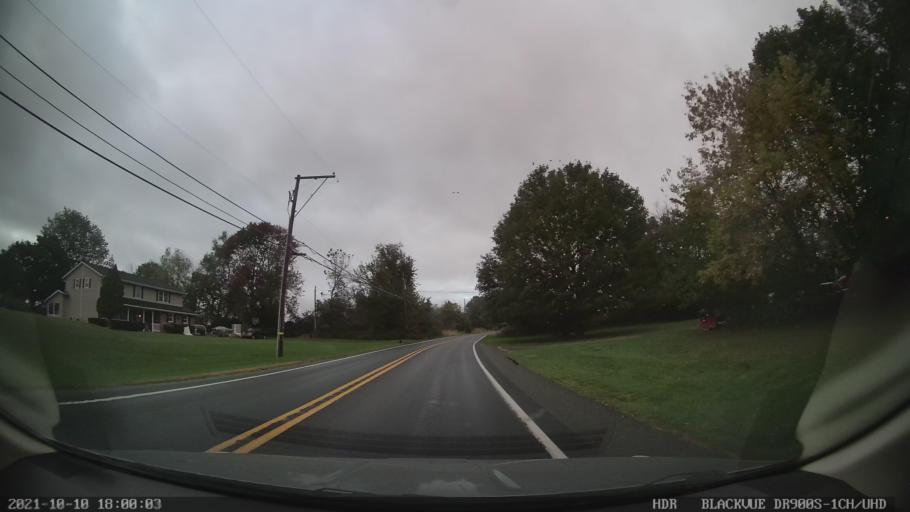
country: US
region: Pennsylvania
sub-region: Lehigh County
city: Egypt
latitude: 40.6432
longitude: -75.5522
